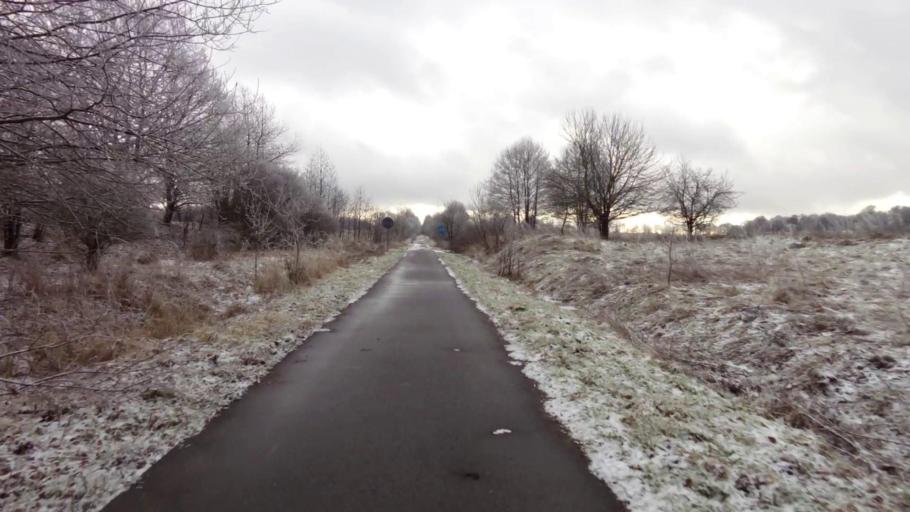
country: PL
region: West Pomeranian Voivodeship
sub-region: Powiat swidwinski
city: Polczyn-Zdroj
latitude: 53.6821
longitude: 16.0312
